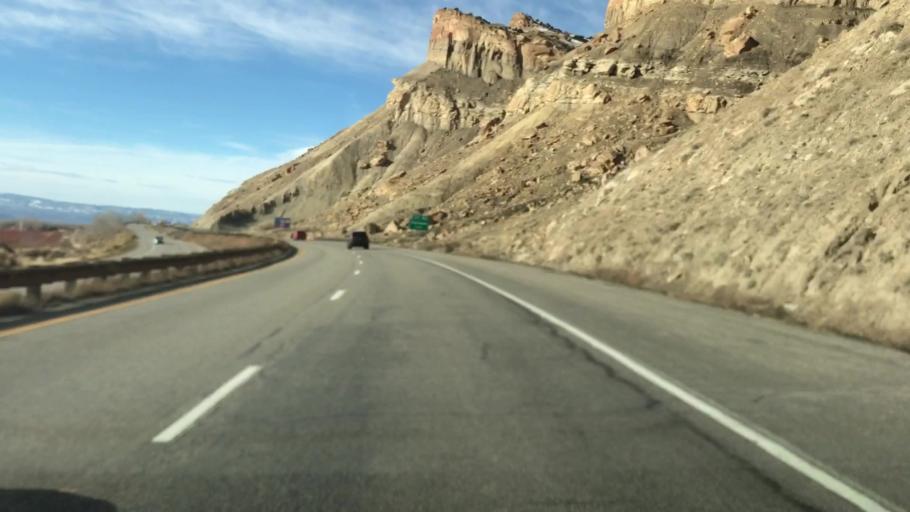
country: US
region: Colorado
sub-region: Mesa County
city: Palisade
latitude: 39.1195
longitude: -108.3391
